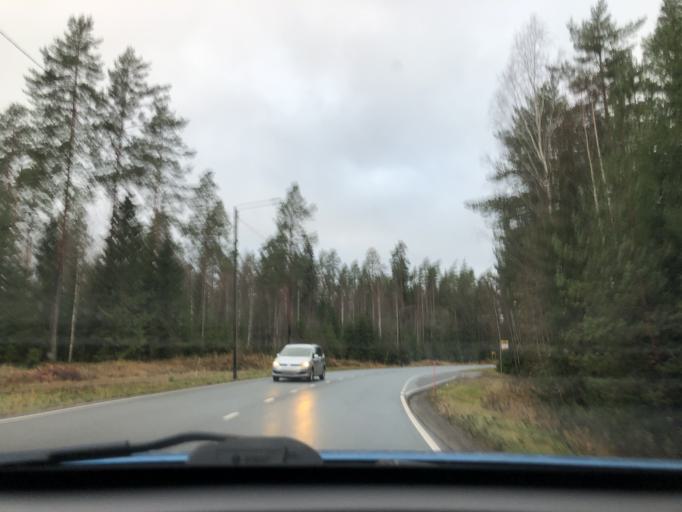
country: FI
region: Pirkanmaa
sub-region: Tampere
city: Kangasala
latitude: 61.5305
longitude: 23.9997
